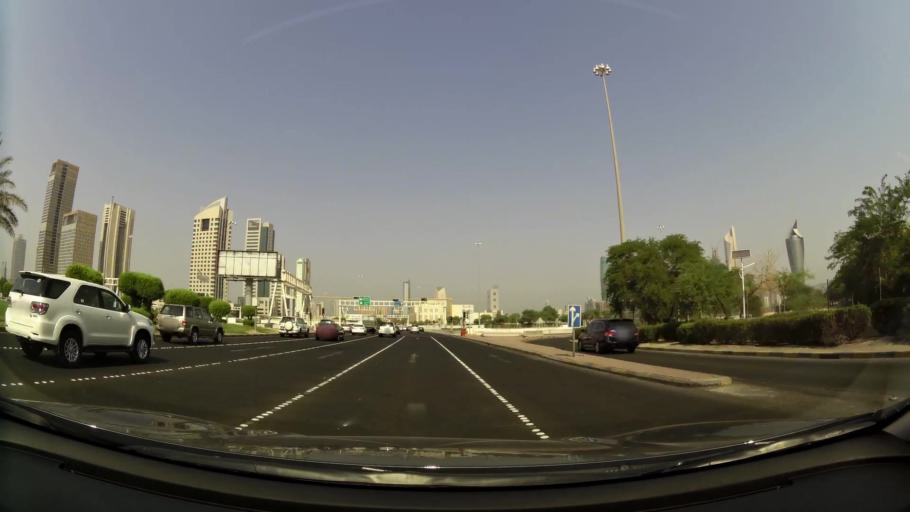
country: KW
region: Al Asimah
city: Kuwait City
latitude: 29.3607
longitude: 47.9878
